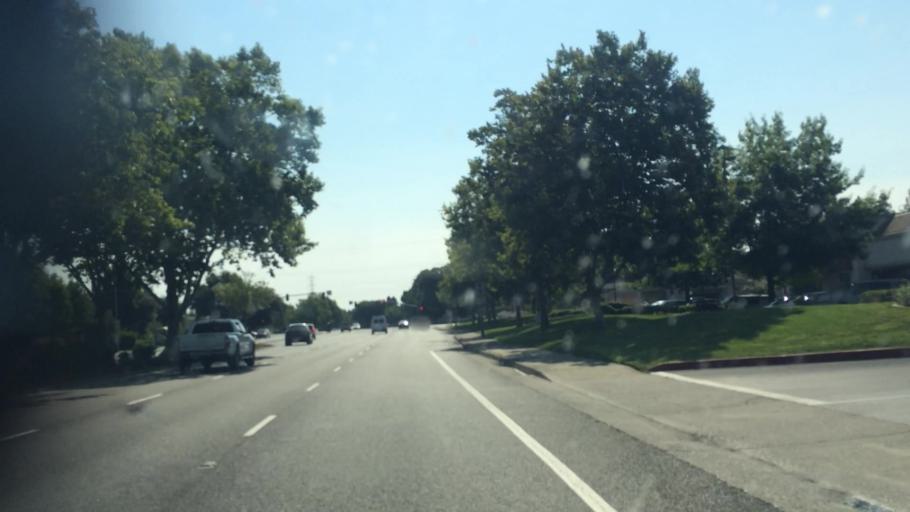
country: US
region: California
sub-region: Sacramento County
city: Laguna
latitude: 38.4231
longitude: -121.4501
